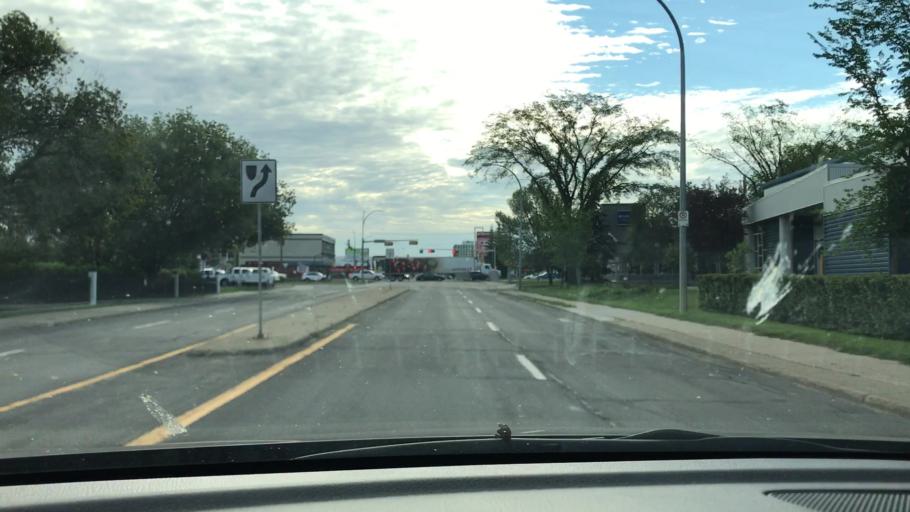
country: CA
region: Alberta
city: Edmonton
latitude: 53.5412
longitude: -113.4458
